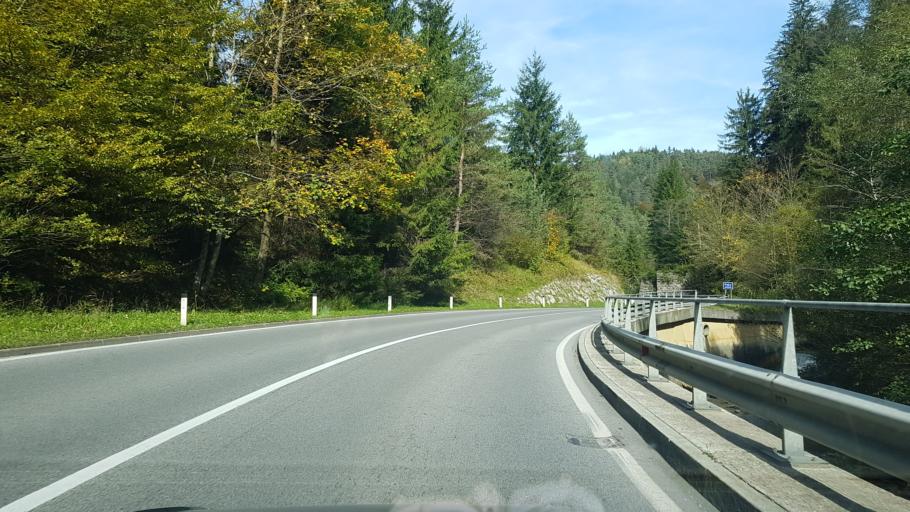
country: SI
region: Velenje
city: Velenje
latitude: 46.4183
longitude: 15.1737
